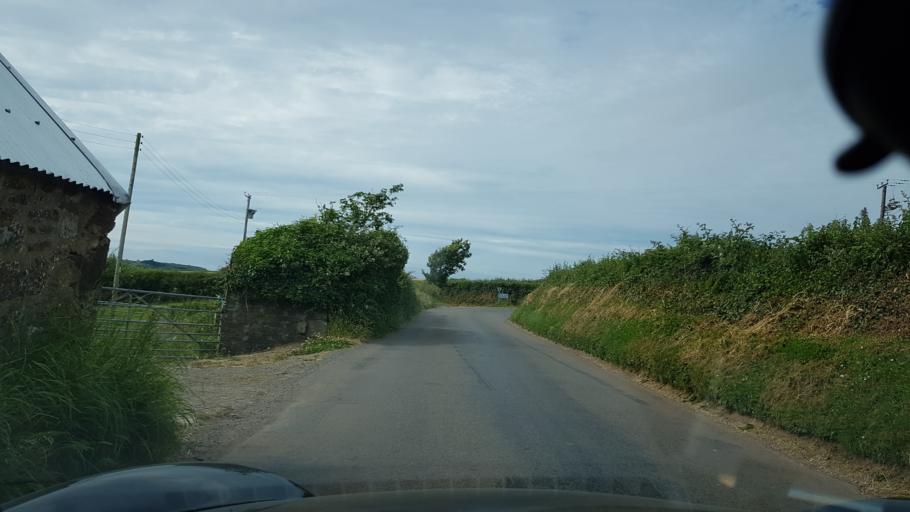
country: GB
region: Wales
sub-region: Pembrokeshire
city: Dale
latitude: 51.7321
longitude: -5.1671
